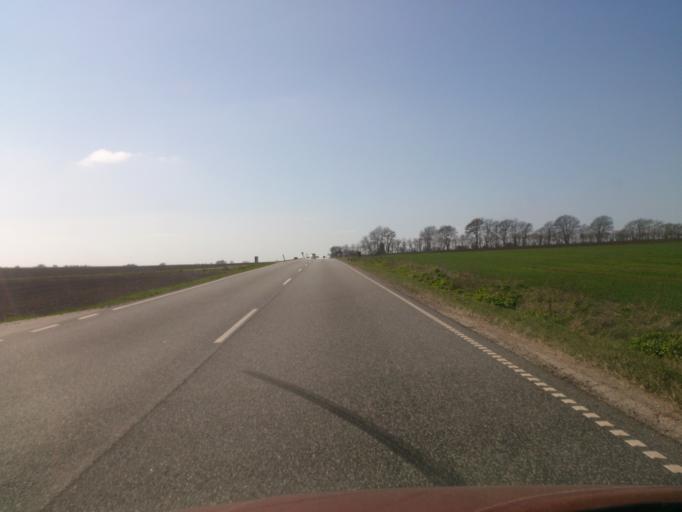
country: DK
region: Central Jutland
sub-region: Favrskov Kommune
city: Ulstrup
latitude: 56.4984
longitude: 9.7933
